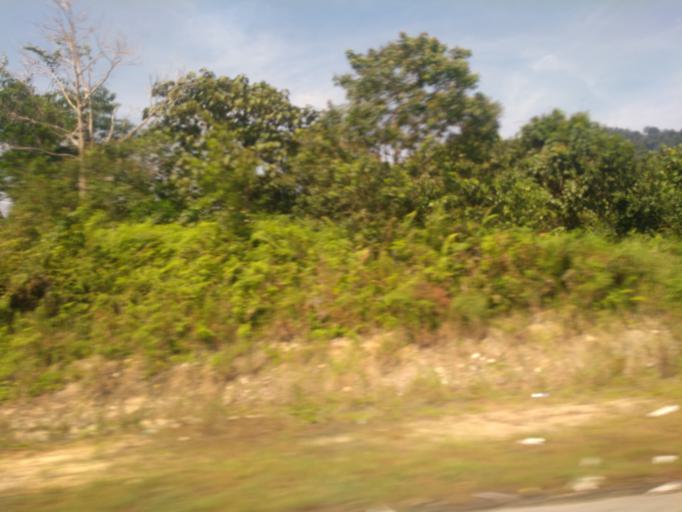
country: MY
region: Sarawak
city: Kuching
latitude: 1.6443
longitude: 110.1907
